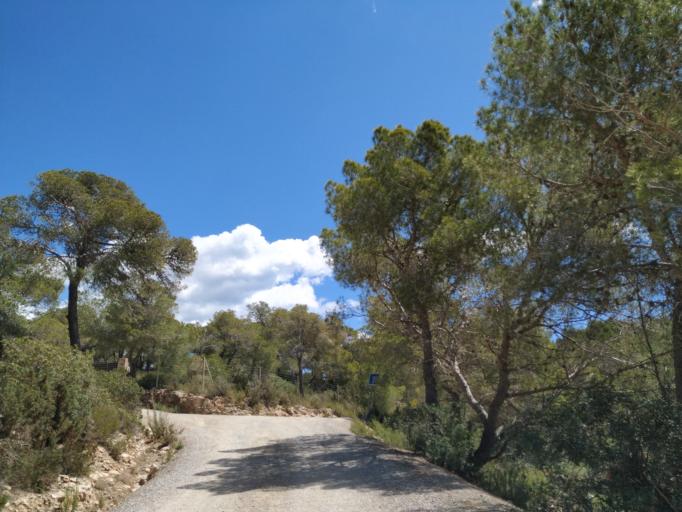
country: ES
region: Balearic Islands
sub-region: Illes Balears
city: Ibiza
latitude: 38.9235
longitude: 1.4756
